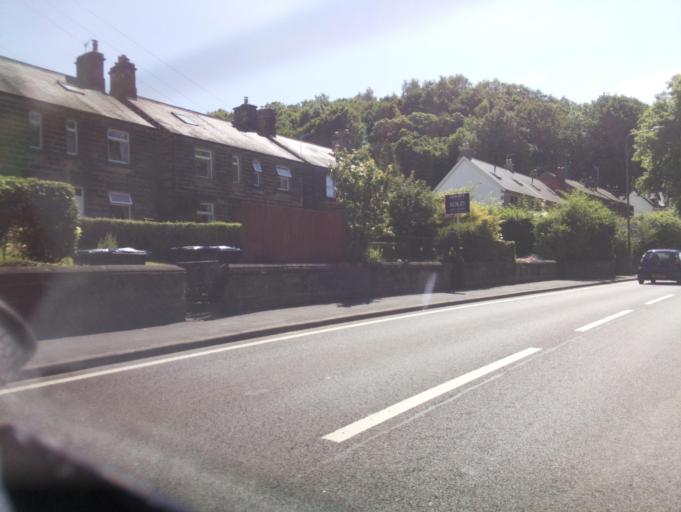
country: GB
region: England
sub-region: Derbyshire
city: Matlock
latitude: 53.1738
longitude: -1.6063
